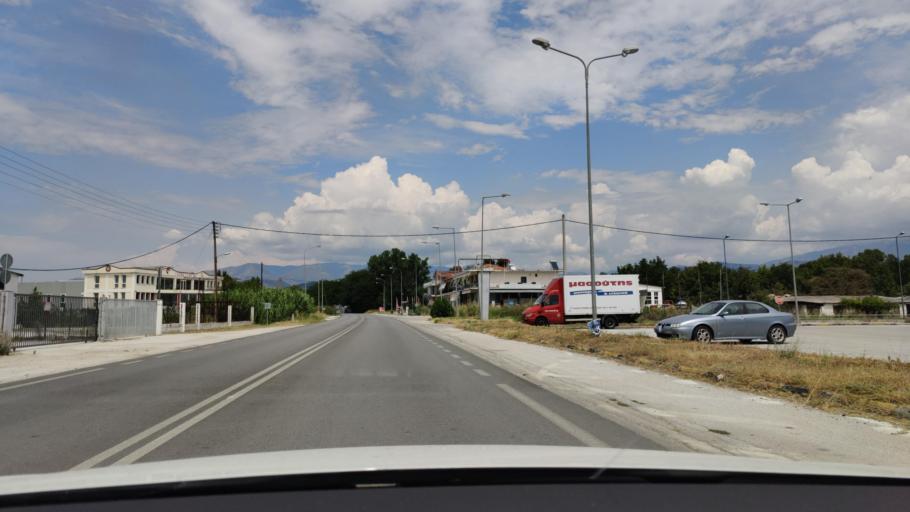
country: GR
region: Central Macedonia
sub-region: Nomos Serron
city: Serres
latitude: 41.0673
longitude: 23.5405
